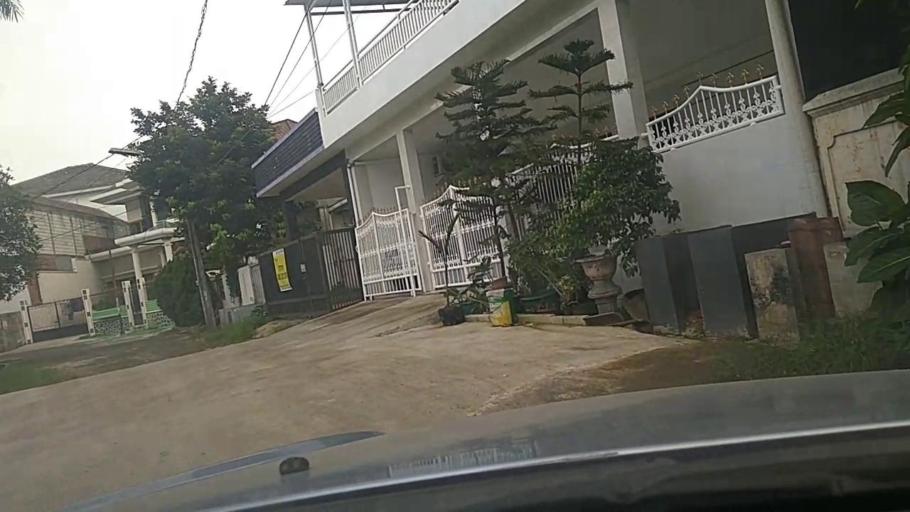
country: ID
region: West Java
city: Pamulang
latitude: -6.3449
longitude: 106.7331
